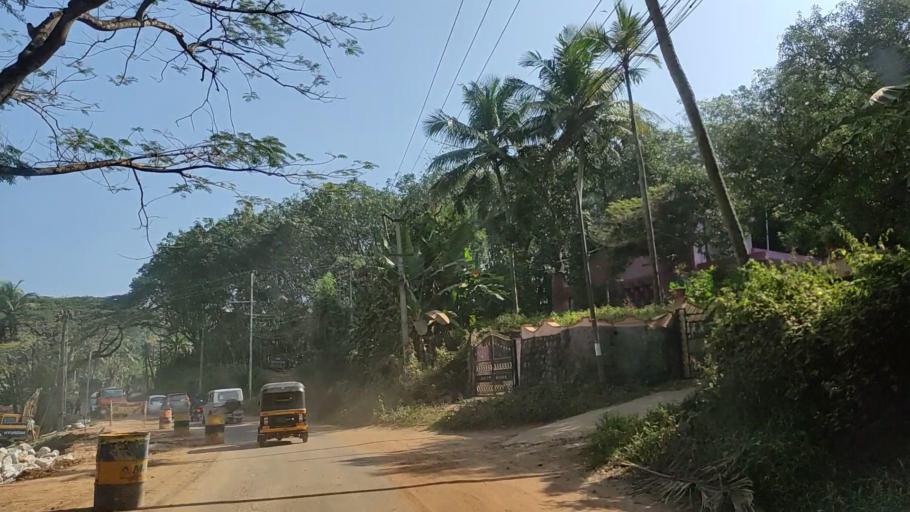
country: IN
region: Kerala
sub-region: Kollam
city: Punalur
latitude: 8.9134
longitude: 76.8848
